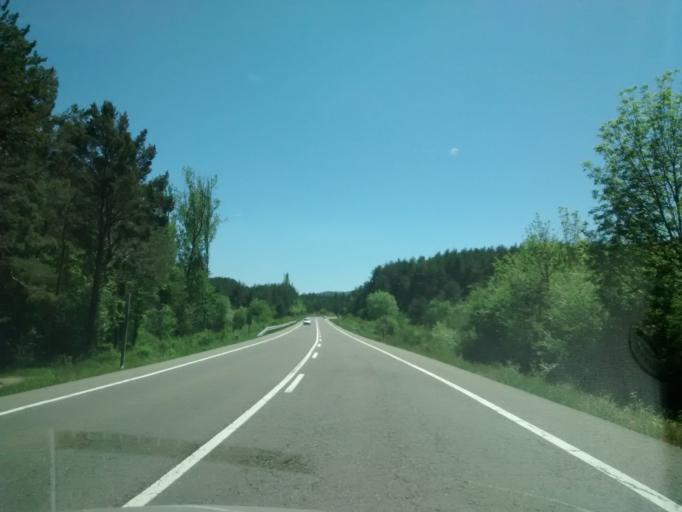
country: ES
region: Aragon
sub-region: Provincia de Huesca
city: Villanua
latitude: 42.6621
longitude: -0.5543
